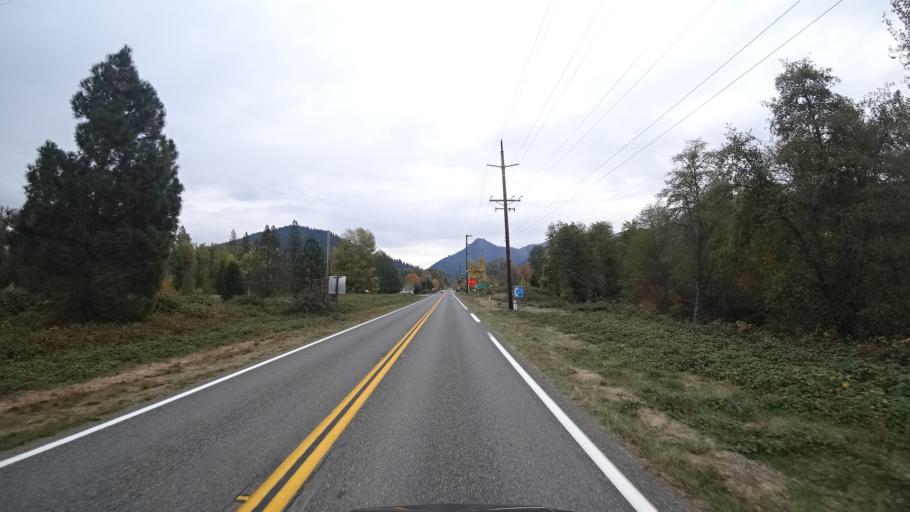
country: US
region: California
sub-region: Siskiyou County
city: Happy Camp
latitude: 41.8440
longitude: -123.2011
